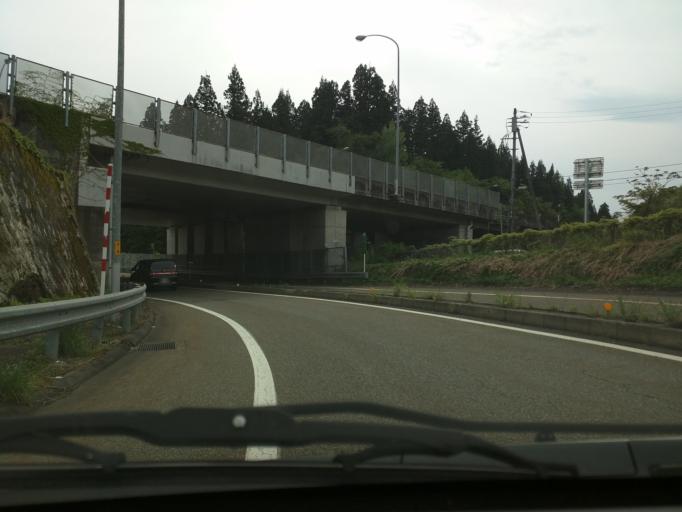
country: JP
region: Niigata
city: Ojiya
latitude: 37.2565
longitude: 138.9245
